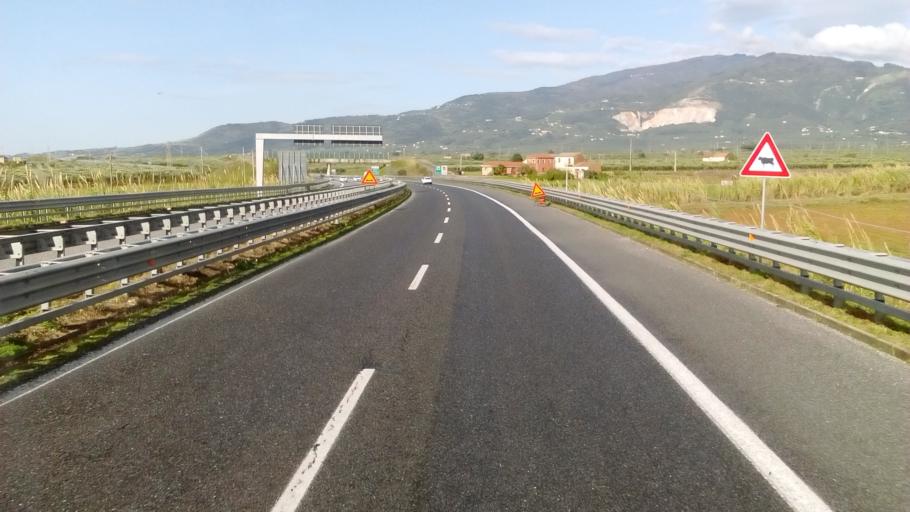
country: IT
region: Calabria
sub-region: Provincia di Catanzaro
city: Santa Eufemia Lamezia
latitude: 38.9207
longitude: 16.2630
